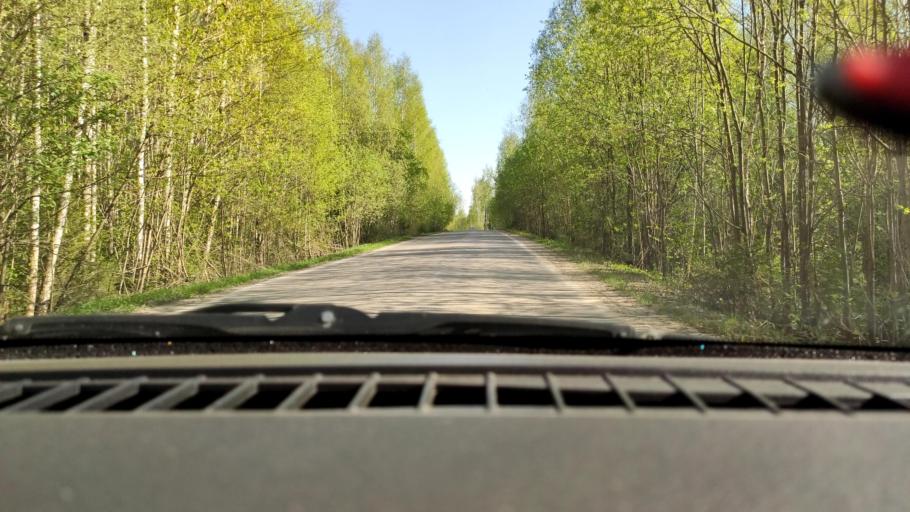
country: RU
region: Perm
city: Kondratovo
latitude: 58.0619
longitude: 56.0031
